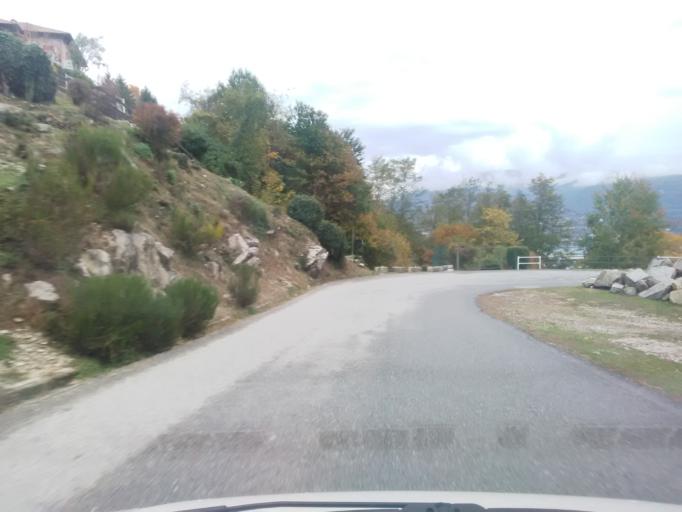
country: IT
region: Piedmont
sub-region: Provincia Verbano-Cusio-Ossola
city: Madonna del Sasso
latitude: 45.7937
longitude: 8.3770
